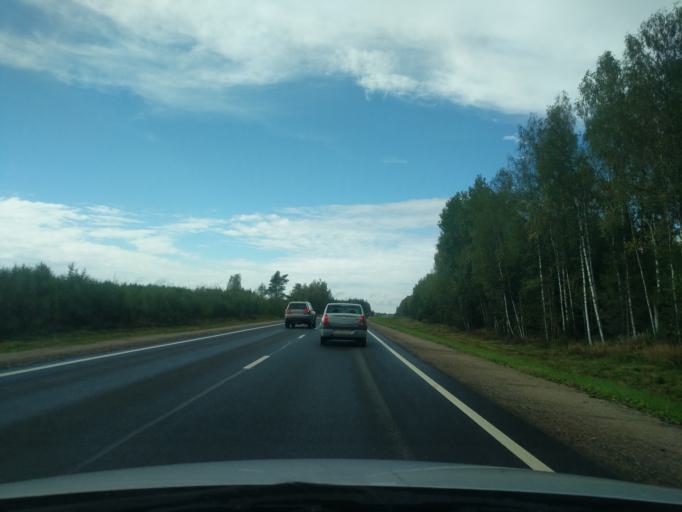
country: RU
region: Kostroma
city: Ostrovskoye
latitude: 57.8140
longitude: 41.9814
